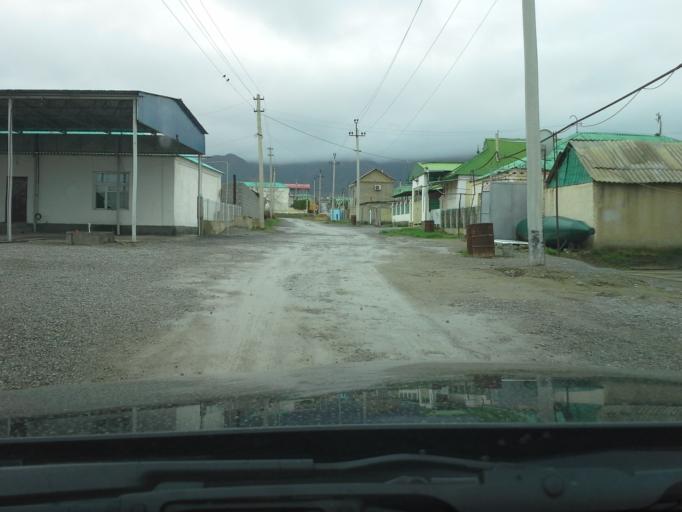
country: TM
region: Ahal
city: Abadan
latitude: 37.9664
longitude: 58.2079
